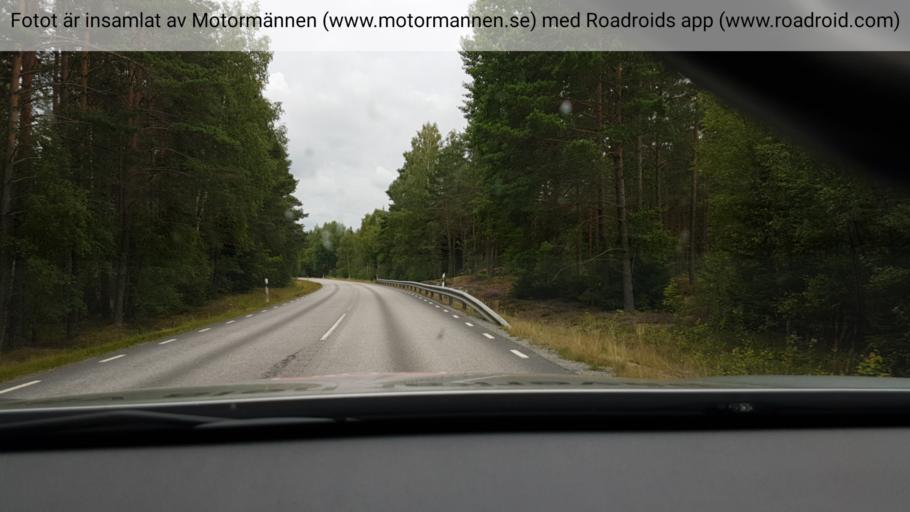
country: SE
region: Stockholm
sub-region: Vallentuna Kommun
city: Vallentuna
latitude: 59.7050
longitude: 18.0453
